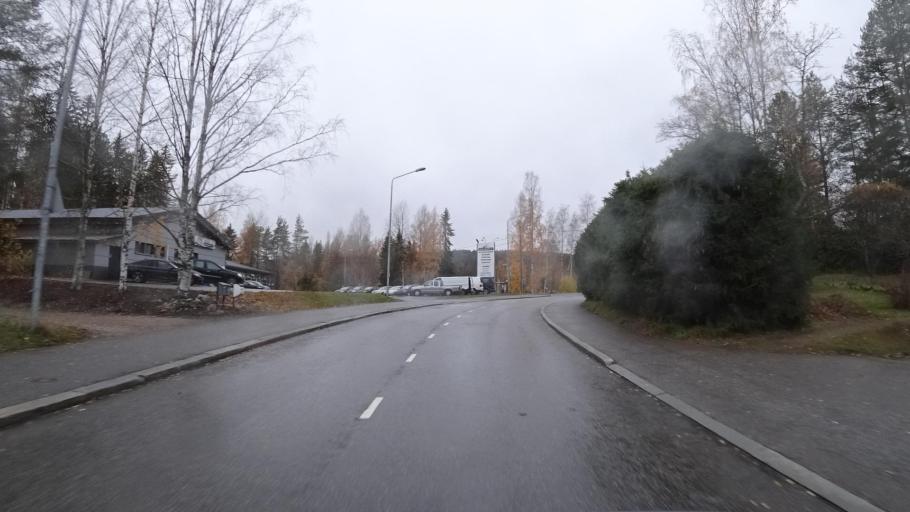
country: FI
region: Northern Savo
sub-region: Kuopio
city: Kuopio
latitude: 62.9227
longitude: 27.6806
